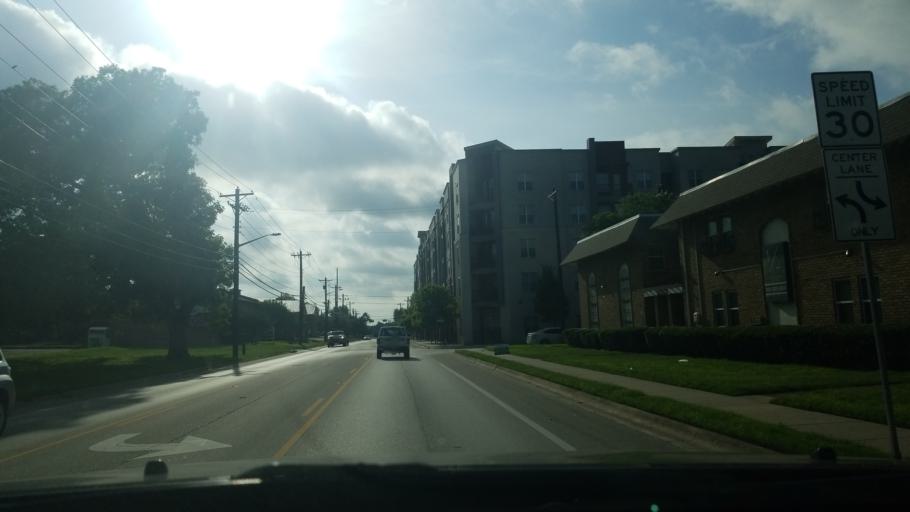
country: US
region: Texas
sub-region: Denton County
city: Denton
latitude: 33.2066
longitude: -97.1438
